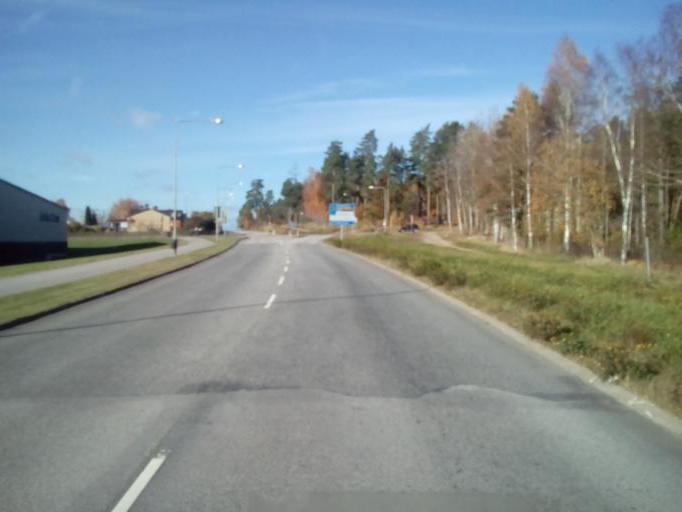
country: SE
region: Kalmar
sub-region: Vimmerby Kommun
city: Vimmerby
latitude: 57.6717
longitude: 15.8730
